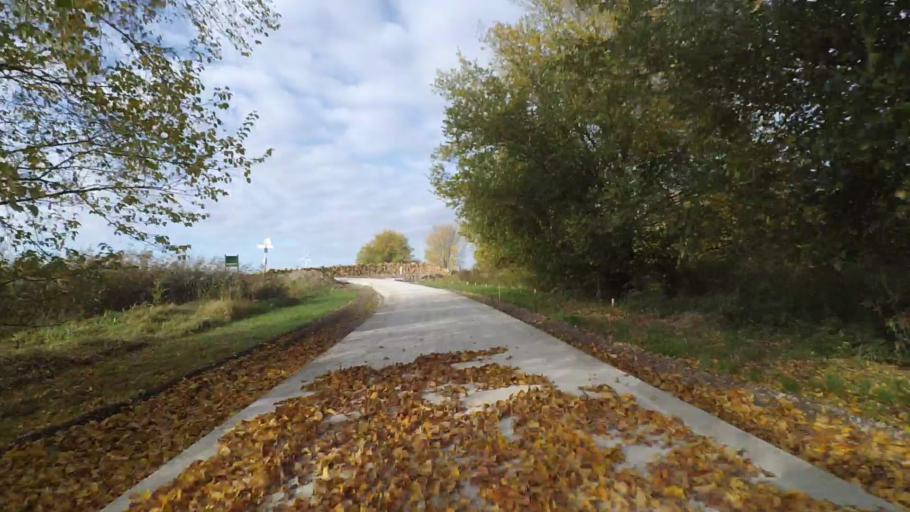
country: NL
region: Utrecht
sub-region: Gemeente Bunschoten
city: Bunschoten
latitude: 52.3308
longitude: 5.4225
